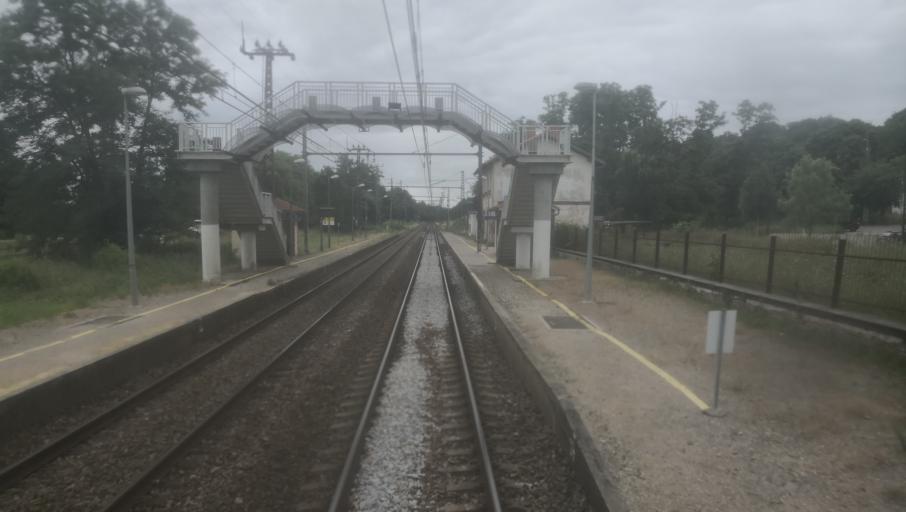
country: FR
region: Midi-Pyrenees
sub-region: Departement du Tarn-et-Garonne
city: Grisolles
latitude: 43.8650
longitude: 1.2764
